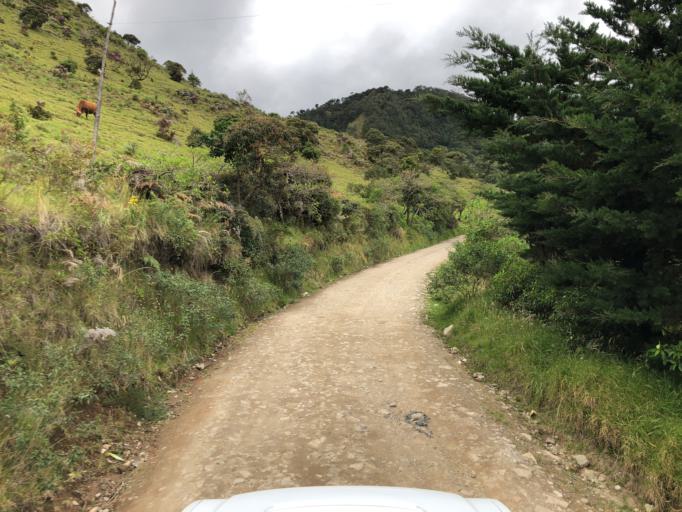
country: CO
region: Cauca
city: Totoro
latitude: 2.5097
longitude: -76.3661
